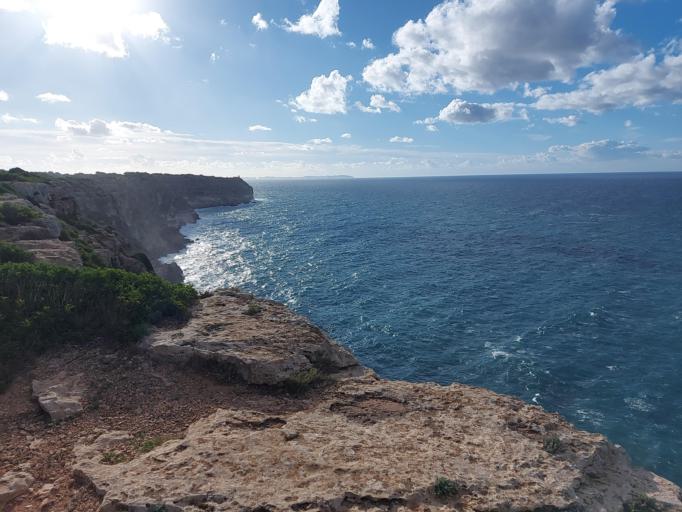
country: ES
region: Balearic Islands
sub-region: Illes Balears
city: s'Arenal
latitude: 39.3773
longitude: 2.7740
